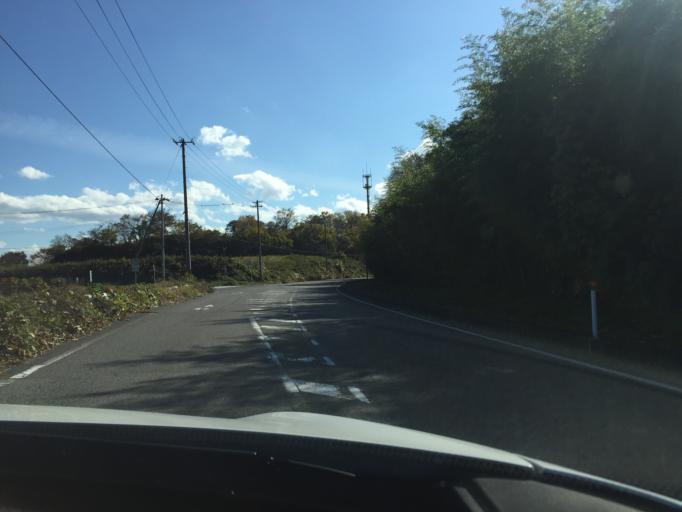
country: JP
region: Fukushima
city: Miharu
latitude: 37.4129
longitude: 140.4836
